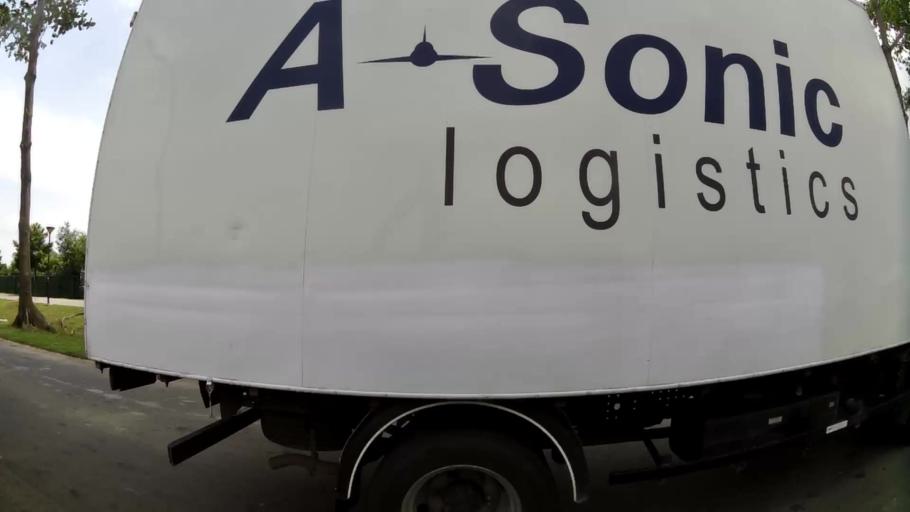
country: SG
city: Singapore
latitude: 1.3409
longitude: 103.9931
